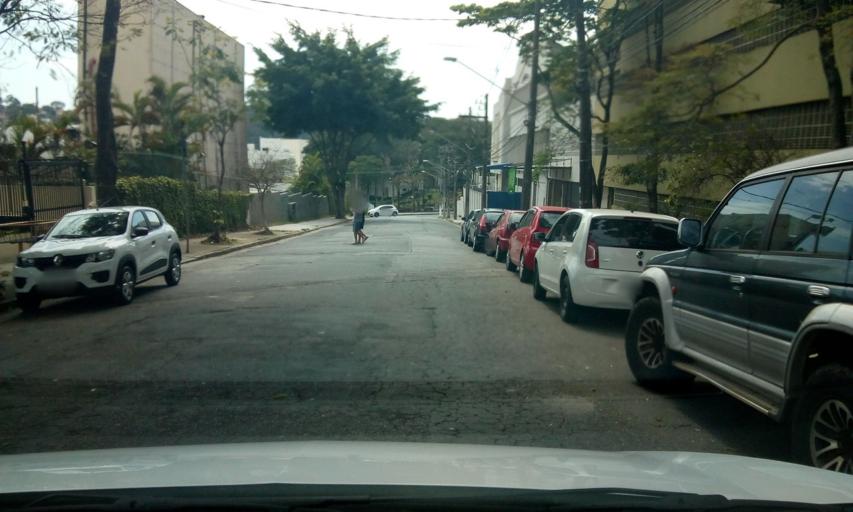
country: BR
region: Sao Paulo
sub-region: Taboao Da Serra
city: Taboao da Serra
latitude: -23.5873
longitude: -46.7221
